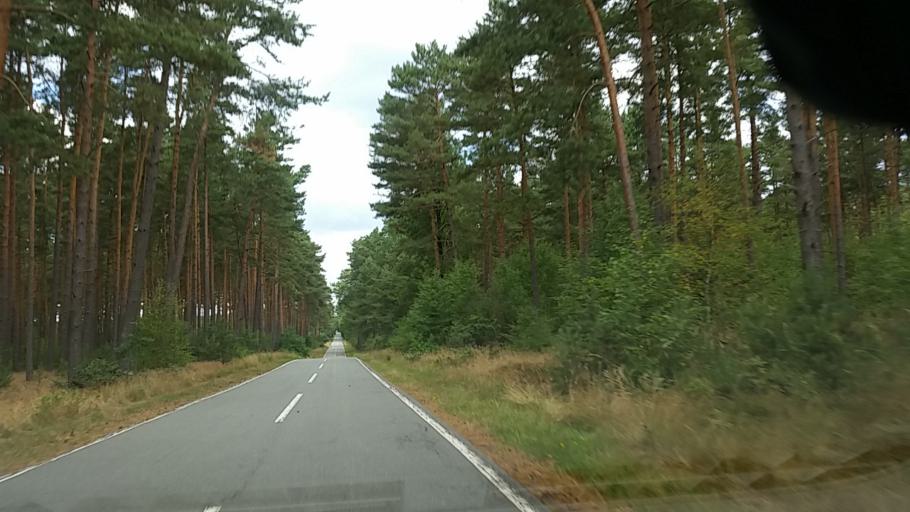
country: DE
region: Lower Saxony
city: Barwedel
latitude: 52.5830
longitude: 10.7855
